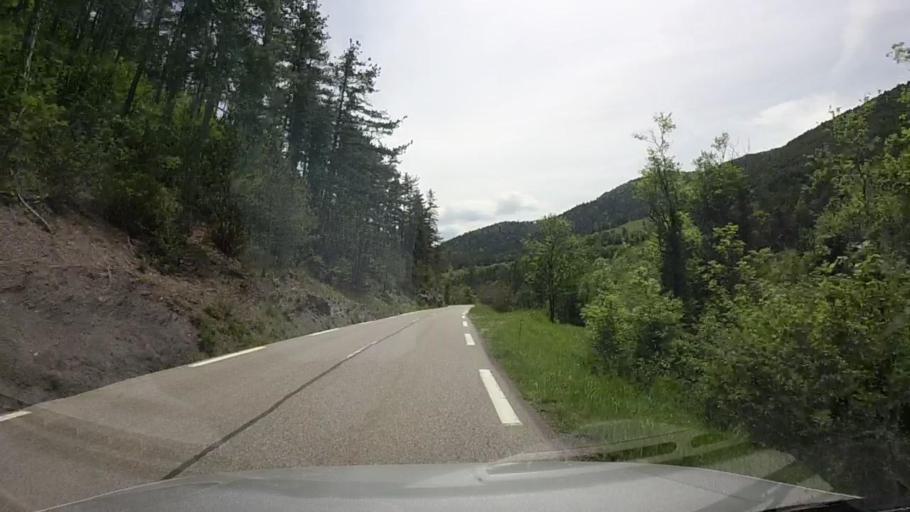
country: FR
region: Provence-Alpes-Cote d'Azur
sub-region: Departement des Alpes-de-Haute-Provence
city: Le Brusquet
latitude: 44.2143
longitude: 6.3629
